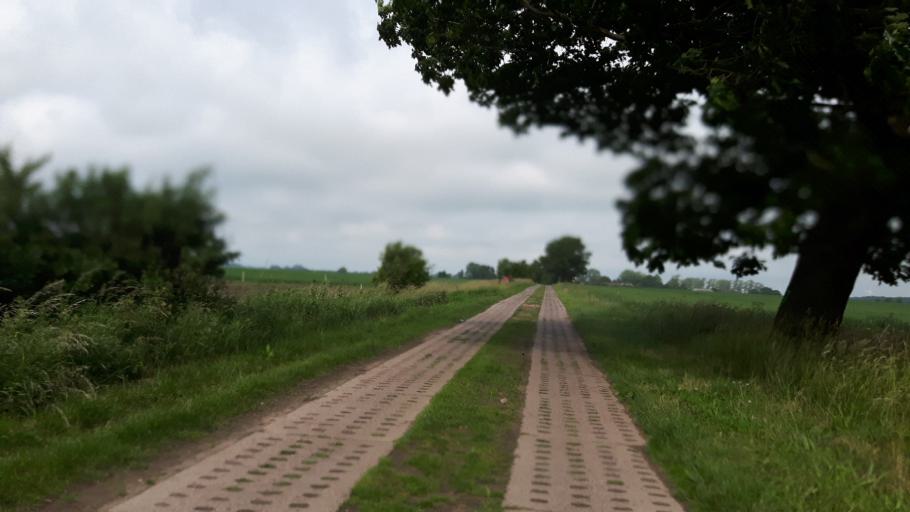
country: PL
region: West Pomeranian Voivodeship
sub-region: Powiat koszalinski
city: Sianow
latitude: 54.2840
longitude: 16.2456
